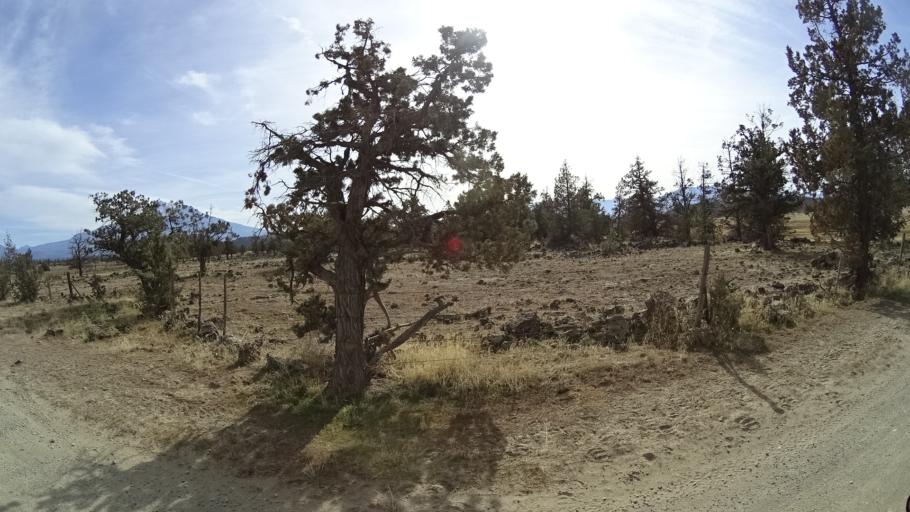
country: US
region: California
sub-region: Siskiyou County
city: Montague
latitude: 41.5952
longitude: -122.4251
